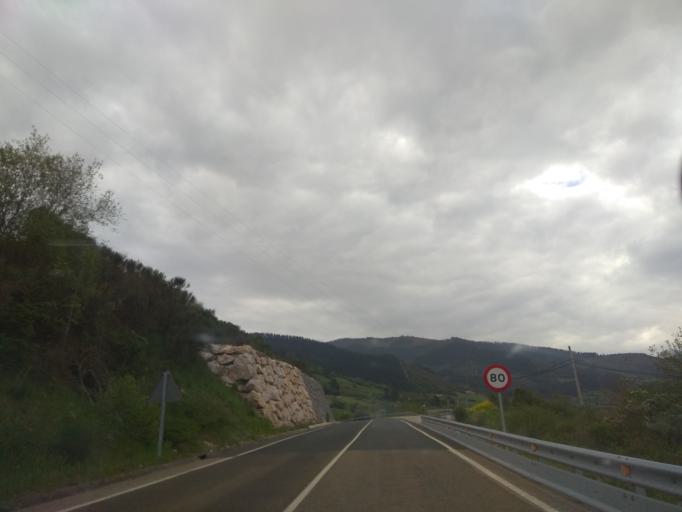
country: ES
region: Cantabria
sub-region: Provincia de Cantabria
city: Potes
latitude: 43.1872
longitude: -4.6049
